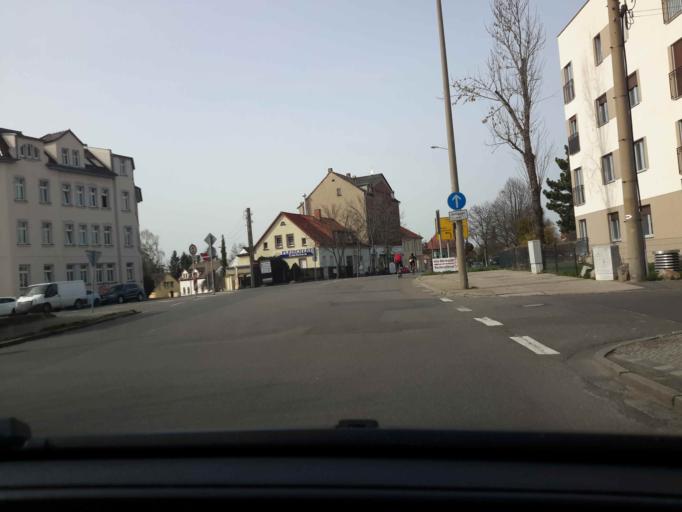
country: DE
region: Saxony
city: Rackwitz
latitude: 51.3959
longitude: 12.3712
